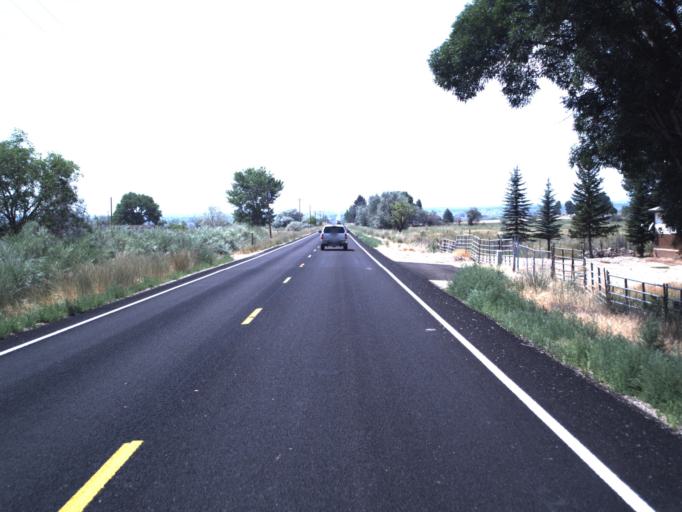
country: US
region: Utah
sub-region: Duchesne County
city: Roosevelt
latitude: 40.4037
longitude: -109.8080
